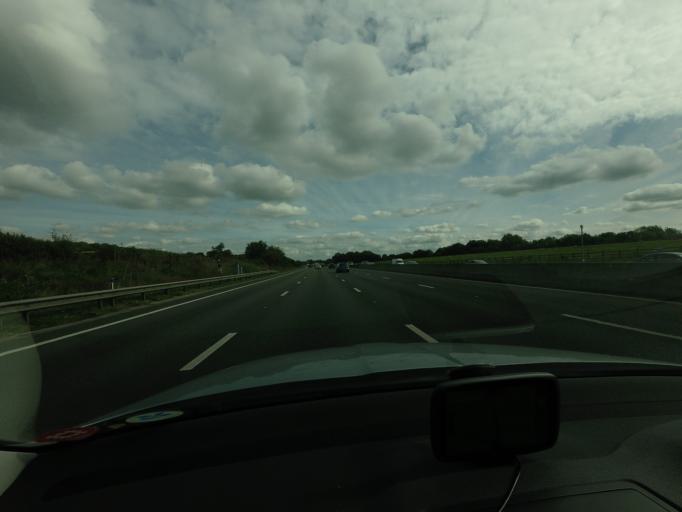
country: GB
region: England
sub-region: Kent
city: Westerham
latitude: 51.2775
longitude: 0.0840
